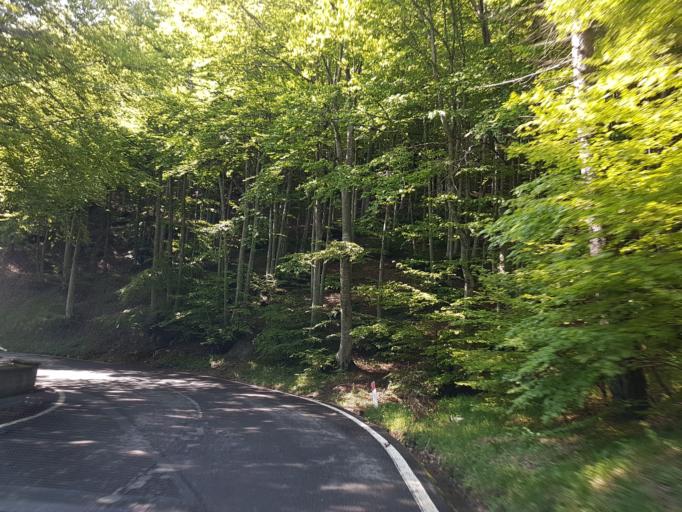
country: IT
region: Emilia-Romagna
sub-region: Forli-Cesena
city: San Piero in Bagno
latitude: 43.7982
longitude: 11.9097
